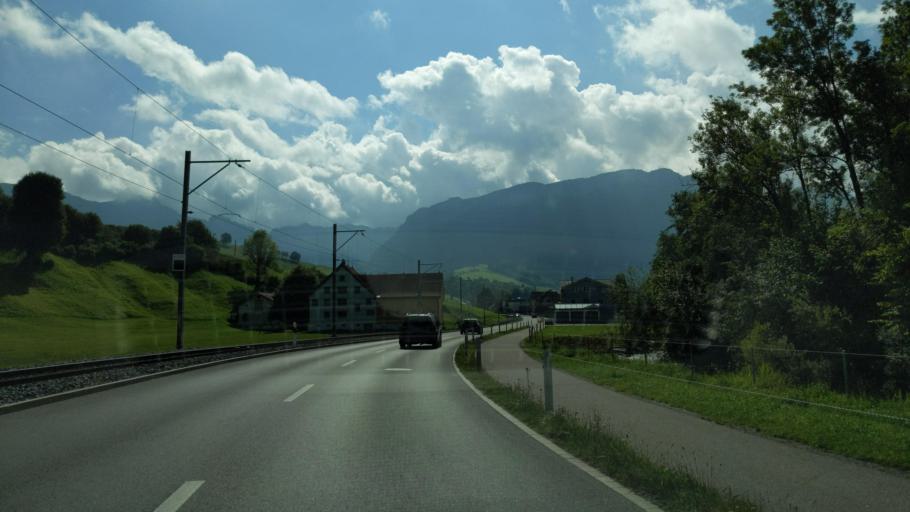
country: CH
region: Appenzell Innerrhoden
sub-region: Appenzell Inner Rhodes
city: Appenzell
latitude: 47.3179
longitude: 9.4331
